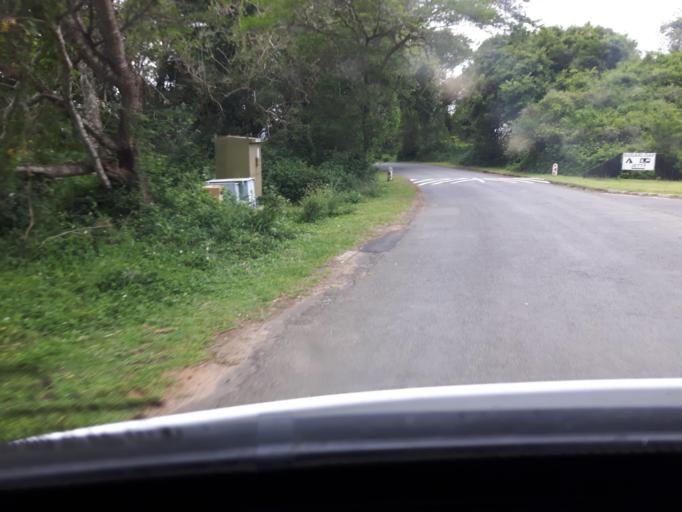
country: ZA
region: KwaZulu-Natal
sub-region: uMkhanyakude District Municipality
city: Mtubatuba
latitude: -28.3870
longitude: 32.4098
